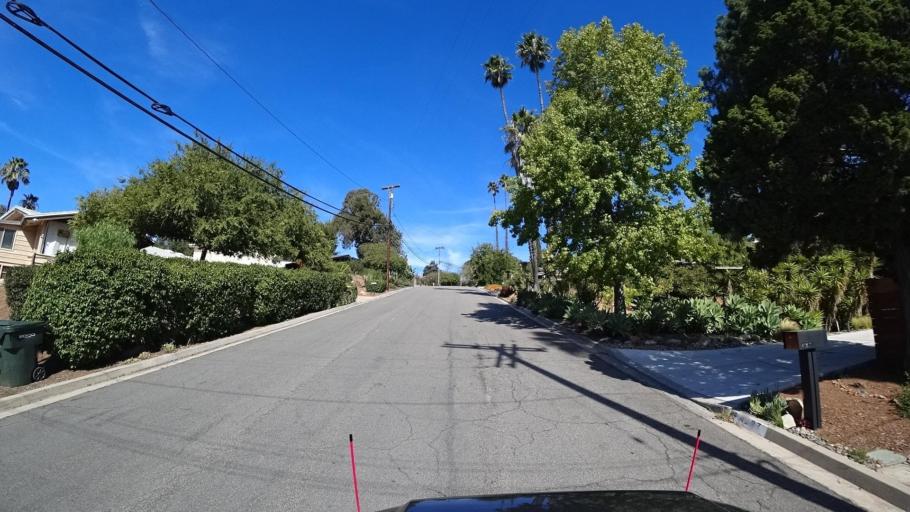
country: US
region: California
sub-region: San Diego County
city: Casa de Oro-Mount Helix
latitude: 32.7554
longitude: -116.9552
